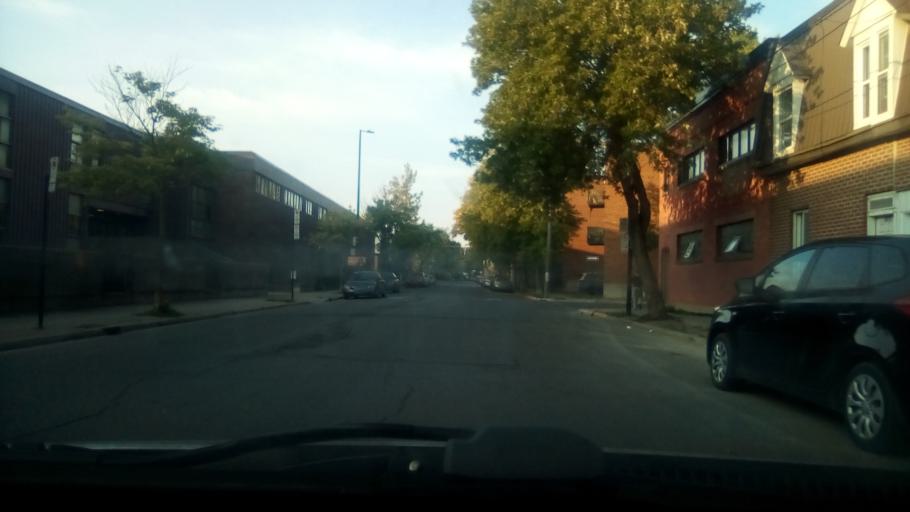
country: CA
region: Quebec
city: Westmount
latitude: 45.4813
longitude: -73.5622
